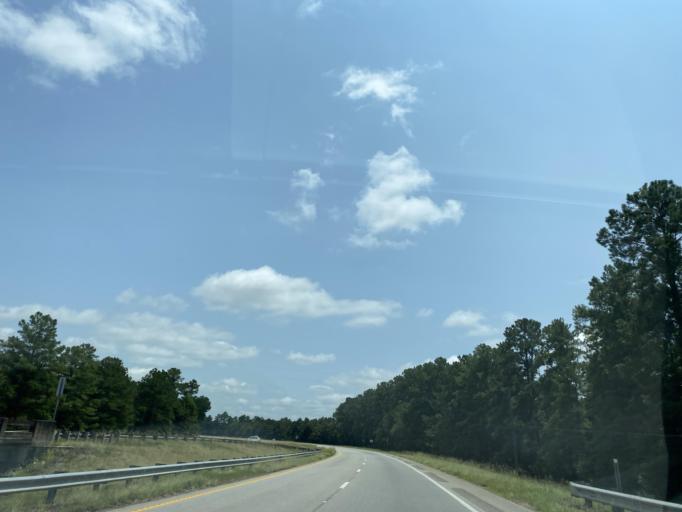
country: US
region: Georgia
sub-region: Telfair County
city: Lumber City
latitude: 31.9105
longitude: -82.6688
